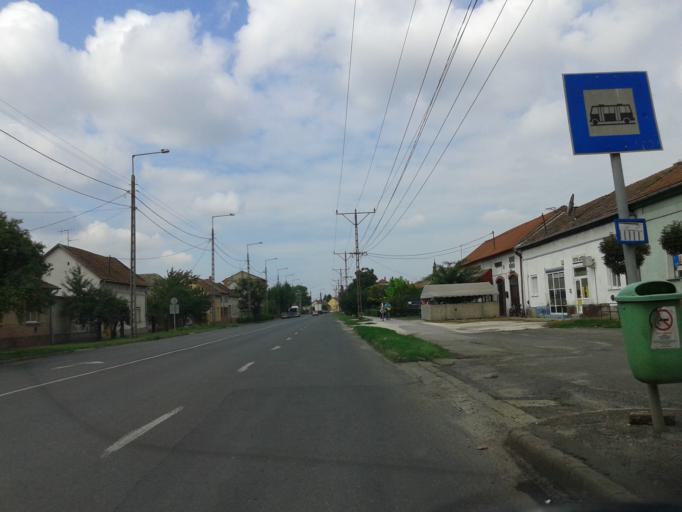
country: HU
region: Csongrad
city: Domaszek
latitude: 46.2736
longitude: 20.0712
